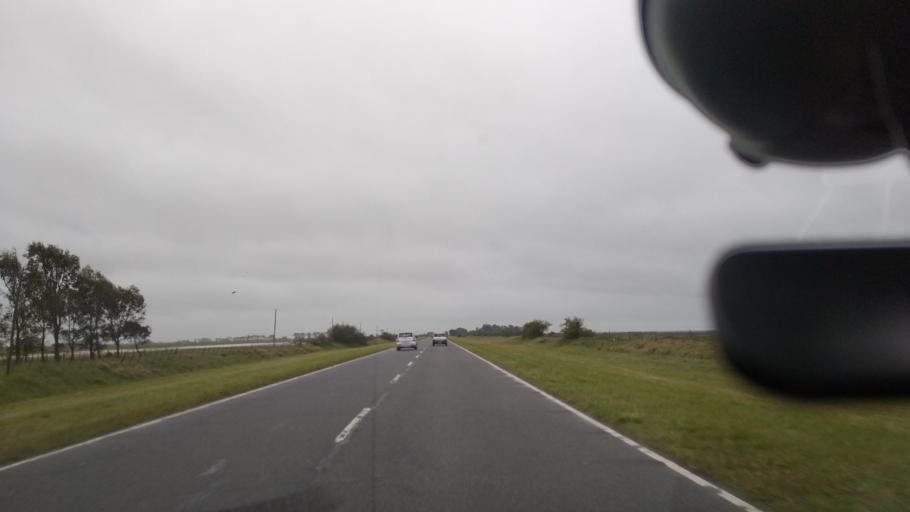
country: AR
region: Buenos Aires
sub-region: Partido de Dolores
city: Dolores
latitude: -36.0668
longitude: -57.4409
